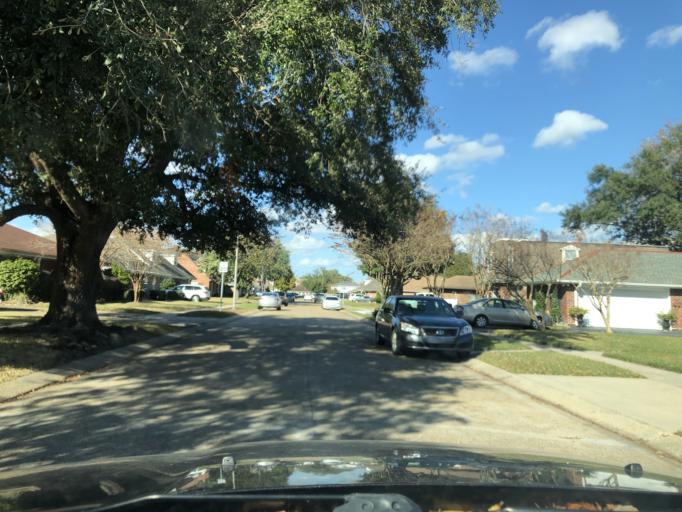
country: US
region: Louisiana
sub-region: Jefferson Parish
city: Metairie Terrace
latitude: 29.9894
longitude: -90.1653
